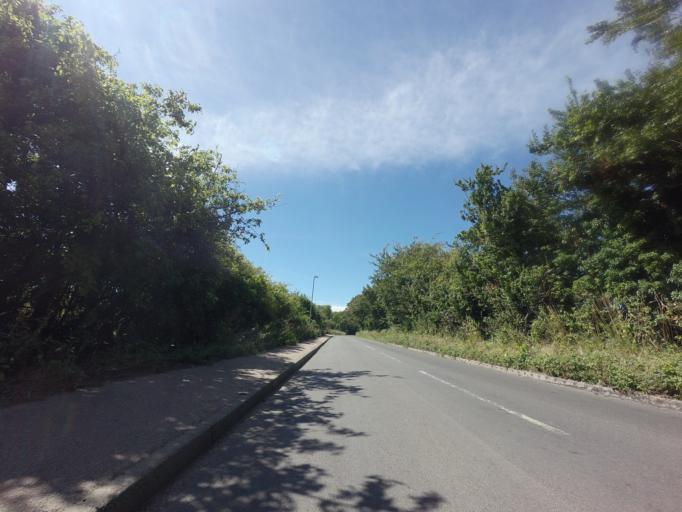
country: GB
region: England
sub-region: Kent
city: Sandwich
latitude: 51.2712
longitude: 1.3558
